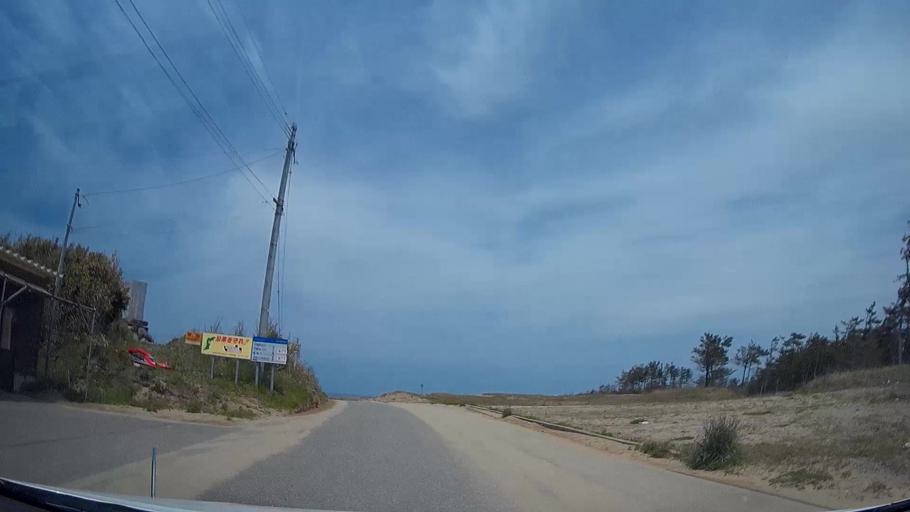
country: JP
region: Ishikawa
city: Hakui
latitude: 36.8383
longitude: 136.7498
